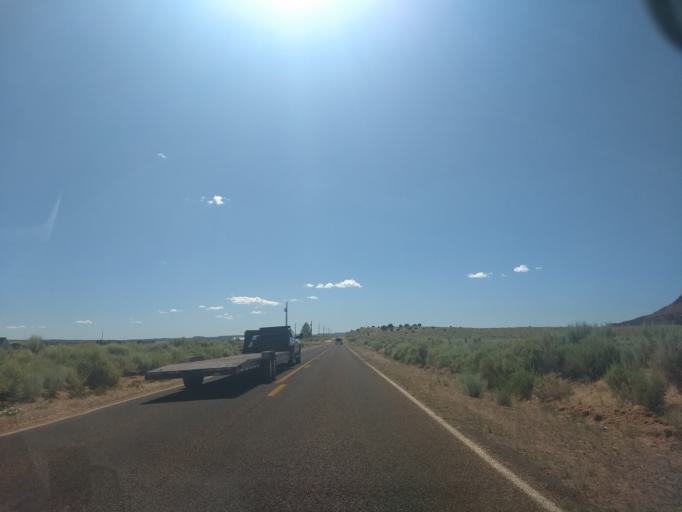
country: US
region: Arizona
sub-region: Mohave County
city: Colorado City
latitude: 36.9469
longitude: -112.9140
